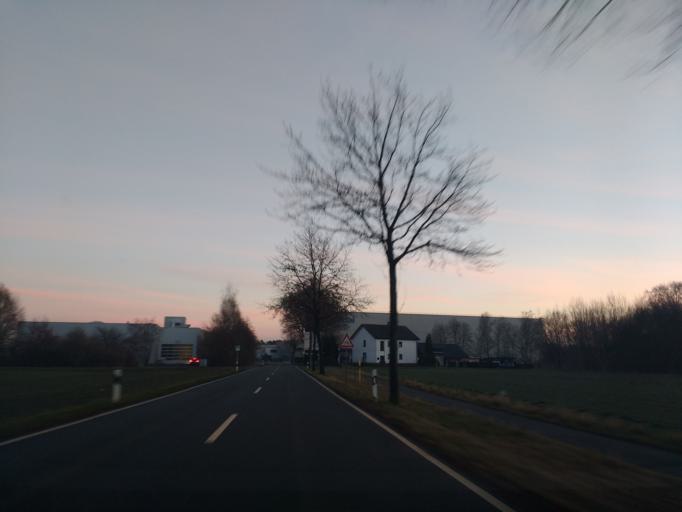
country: DE
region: North Rhine-Westphalia
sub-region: Regierungsbezirk Detmold
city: Hovelhof
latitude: 51.8412
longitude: 8.6459
